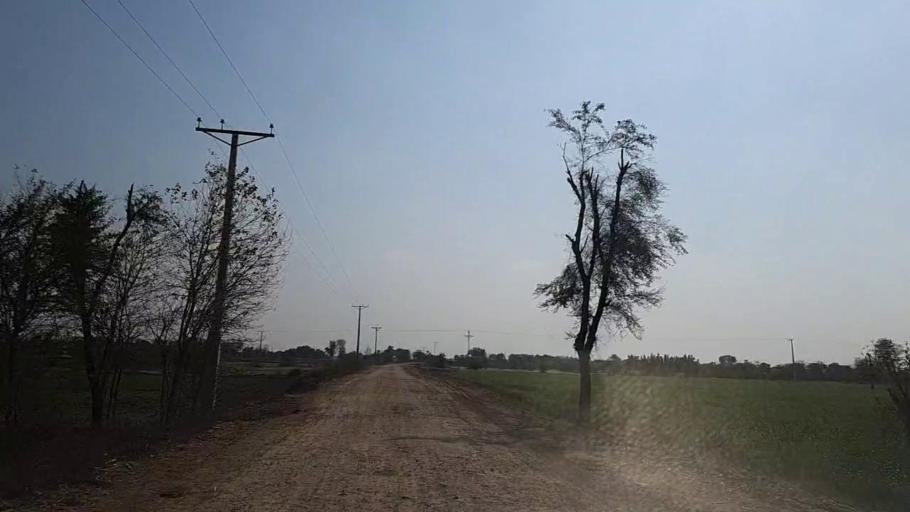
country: PK
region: Sindh
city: Daur
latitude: 26.4548
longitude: 68.2348
